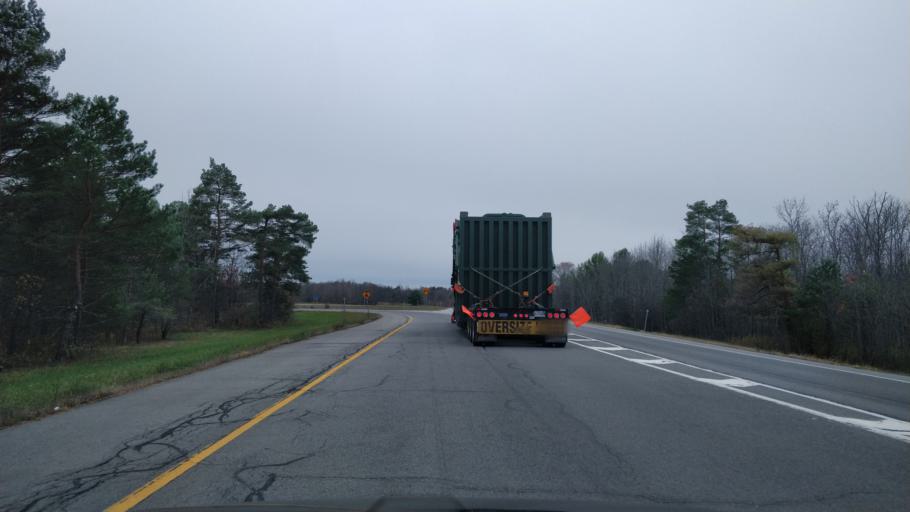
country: CA
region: Ontario
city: Brockville
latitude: 44.5751
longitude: -75.6458
